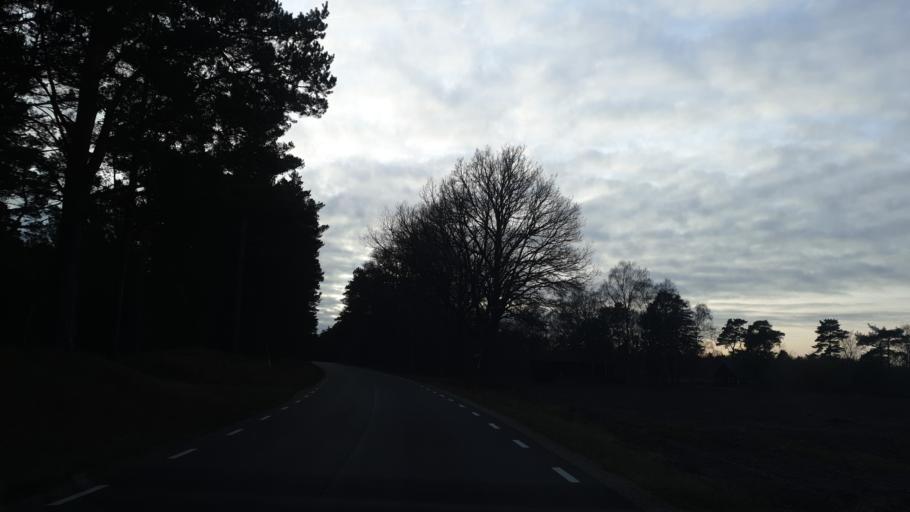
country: SE
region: Kalmar
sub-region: Torsas Kommun
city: Torsas
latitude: 56.2534
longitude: 16.0087
